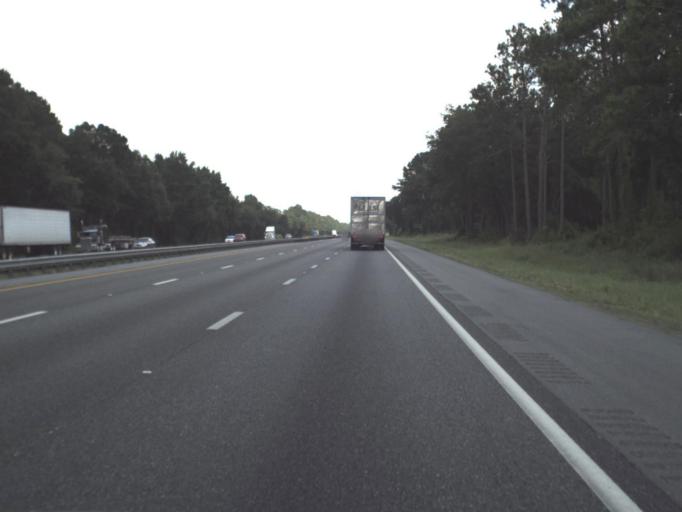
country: US
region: Florida
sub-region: Hamilton County
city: Jasper
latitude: 30.4684
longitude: -82.9657
